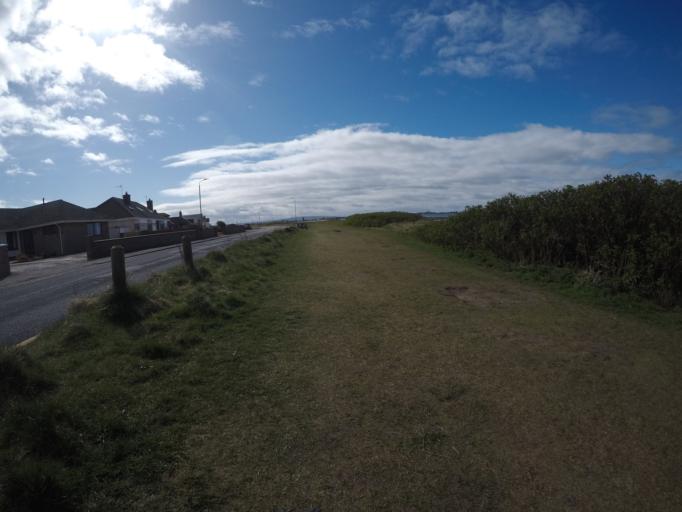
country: GB
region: Scotland
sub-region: South Ayrshire
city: Troon
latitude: 55.5668
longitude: -4.6582
